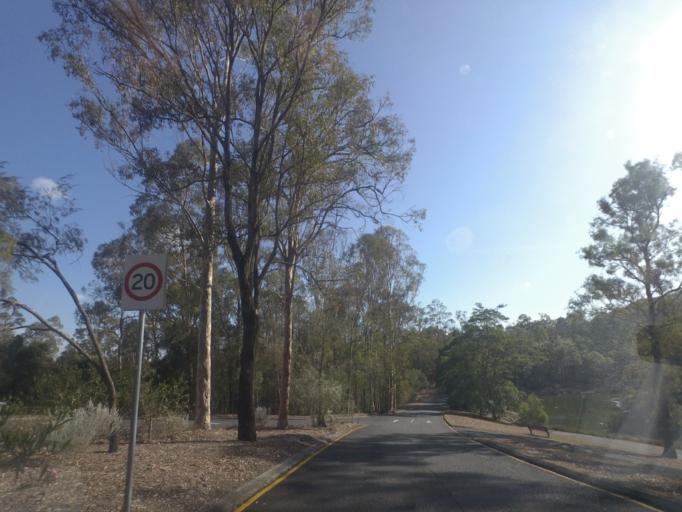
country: AU
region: Queensland
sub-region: Brisbane
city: Taringa
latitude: -27.4796
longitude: 152.9721
